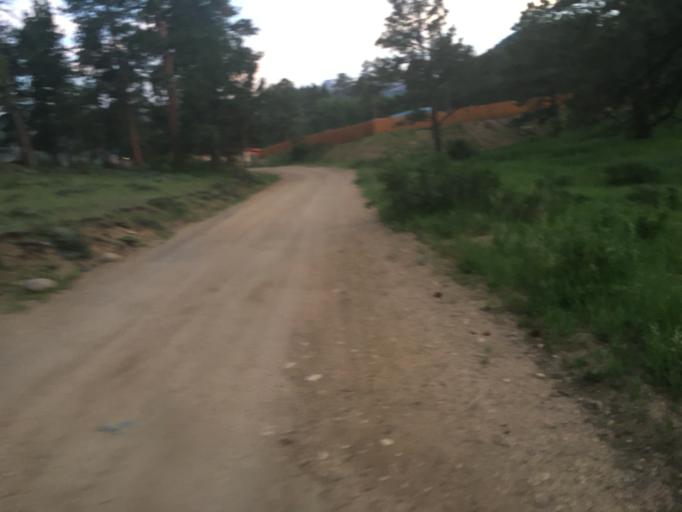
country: US
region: Colorado
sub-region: Larimer County
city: Estes Park
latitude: 40.3450
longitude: -105.5720
